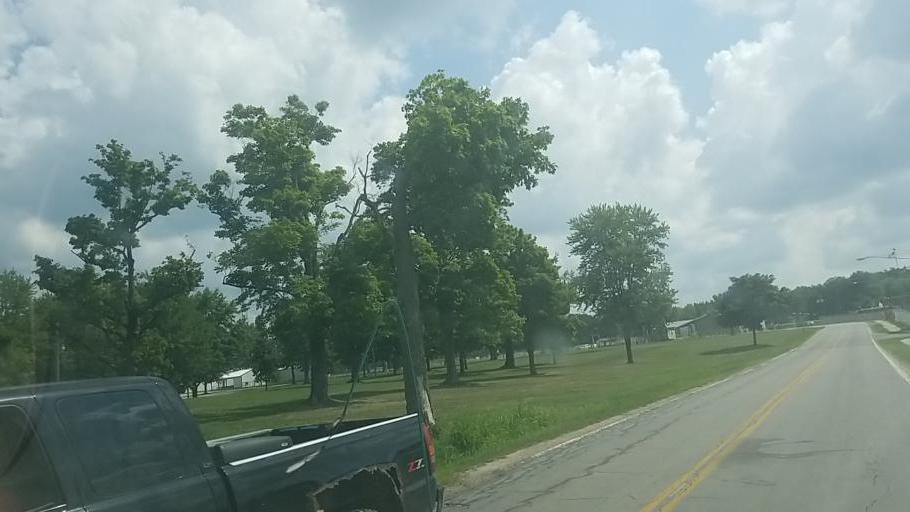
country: US
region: Ohio
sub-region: Wyandot County
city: Upper Sandusky
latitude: 40.8422
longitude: -83.2804
